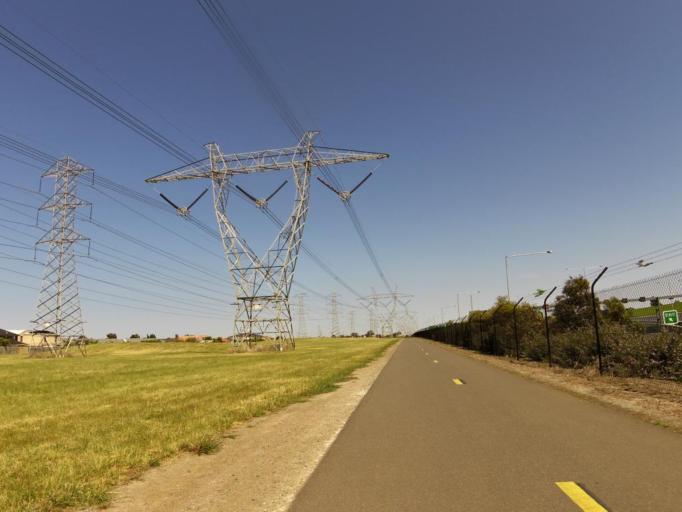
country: AU
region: Victoria
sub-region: Moreland
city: Gowanbrae
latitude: -37.6999
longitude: 144.8964
